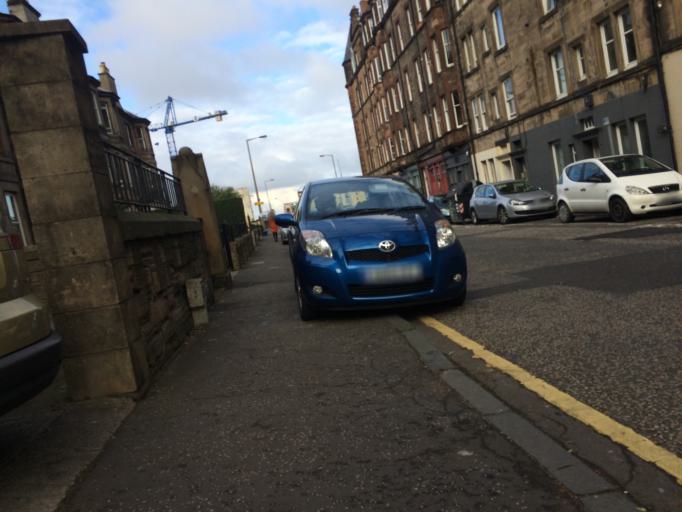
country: GB
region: Scotland
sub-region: Edinburgh
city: Edinburgh
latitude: 55.9399
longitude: -3.2123
